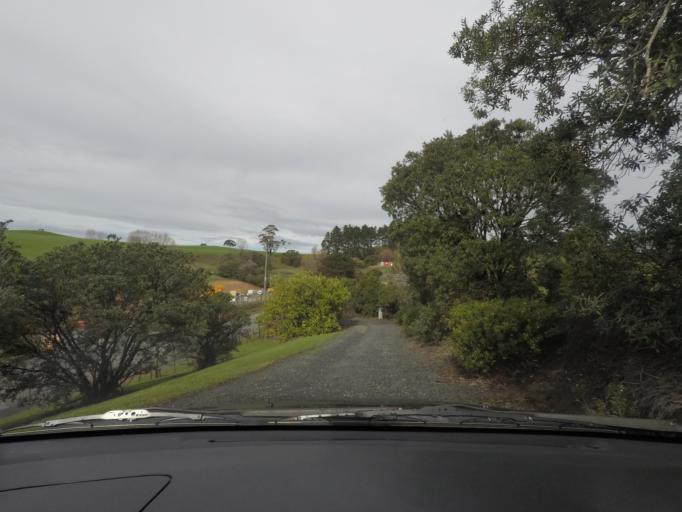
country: NZ
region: Auckland
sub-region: Auckland
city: Warkworth
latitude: -36.4510
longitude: 174.7499
